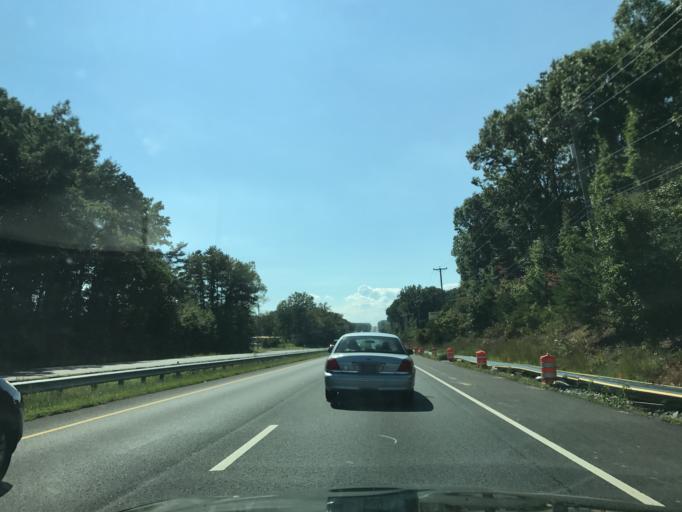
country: US
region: Maryland
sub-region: Cecil County
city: Charlestown
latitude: 39.6001
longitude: -75.9708
